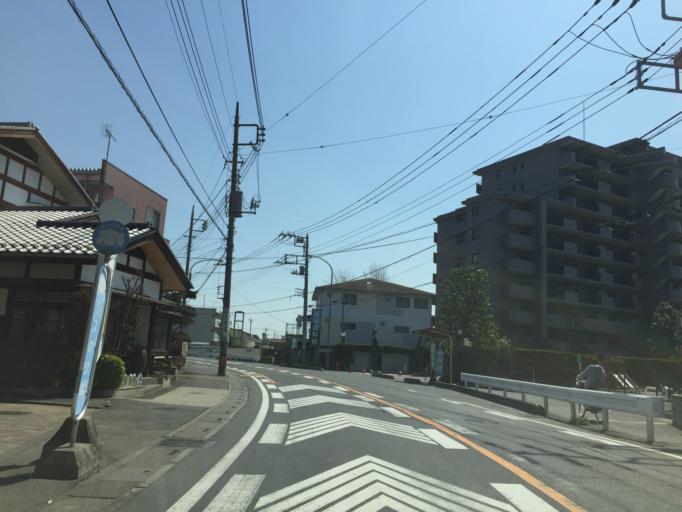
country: JP
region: Saitama
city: Yono
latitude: 35.8519
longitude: 139.6282
